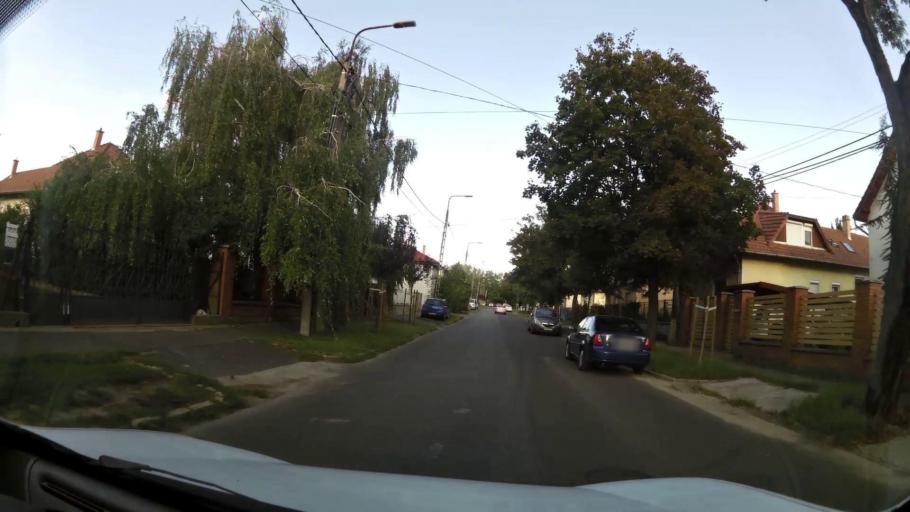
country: HU
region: Budapest
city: Budapest XVI. keruelet
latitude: 47.5026
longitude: 19.1650
